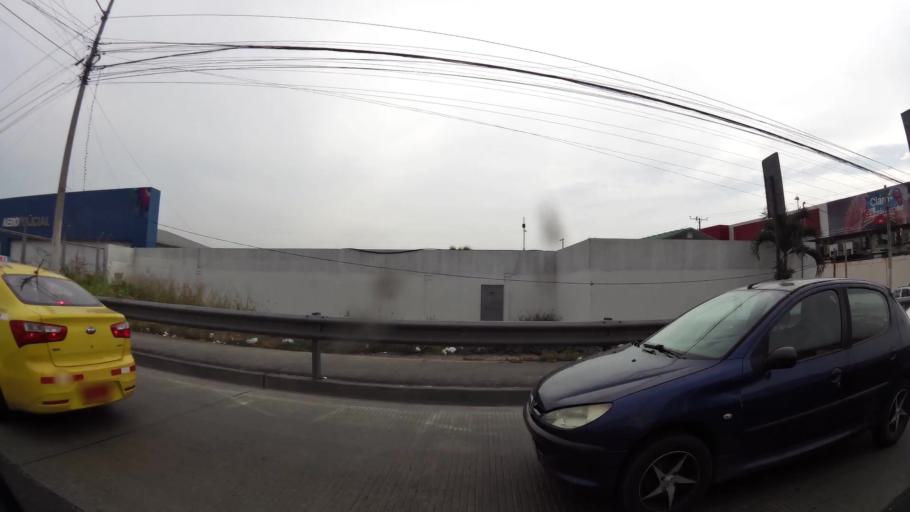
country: EC
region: Guayas
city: Eloy Alfaro
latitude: -2.1534
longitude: -79.8785
